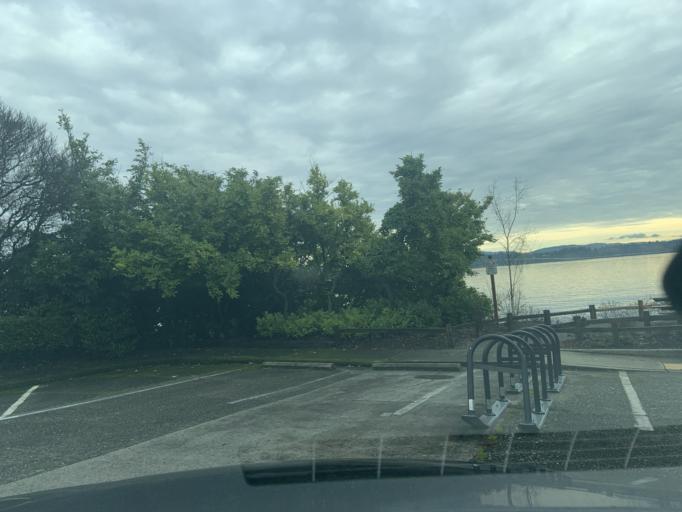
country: US
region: Washington
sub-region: King County
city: Yarrow Point
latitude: 47.6559
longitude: -122.2722
